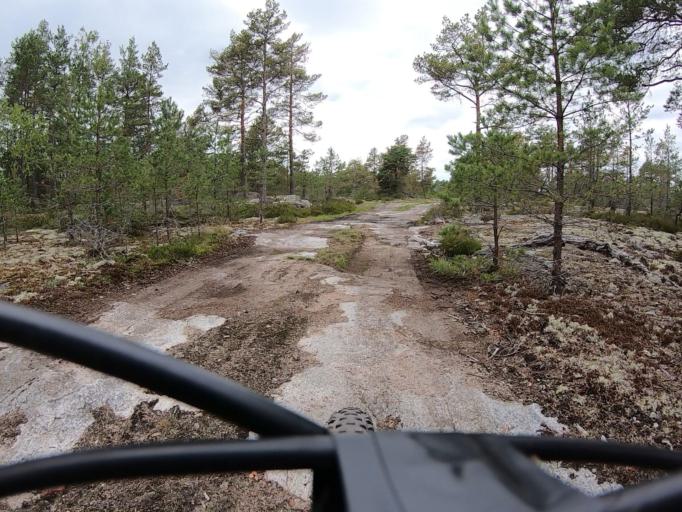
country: FI
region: Varsinais-Suomi
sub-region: Vakka-Suomi
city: Uusikaupunki
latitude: 60.8495
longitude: 21.4178
